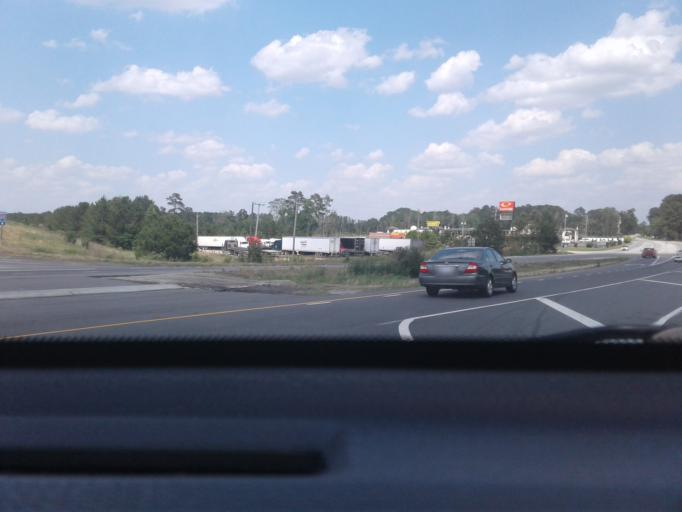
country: US
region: North Carolina
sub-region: Cumberland County
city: Eastover
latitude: 35.1227
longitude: -78.7524
